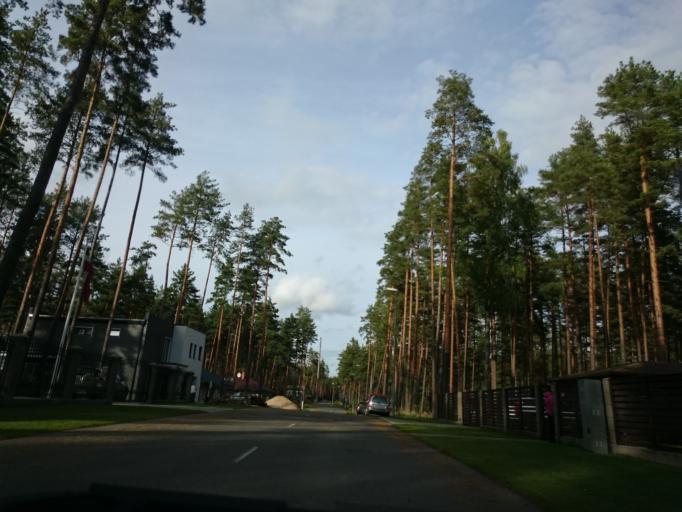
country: LV
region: Adazi
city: Adazi
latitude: 57.0536
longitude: 24.3602
